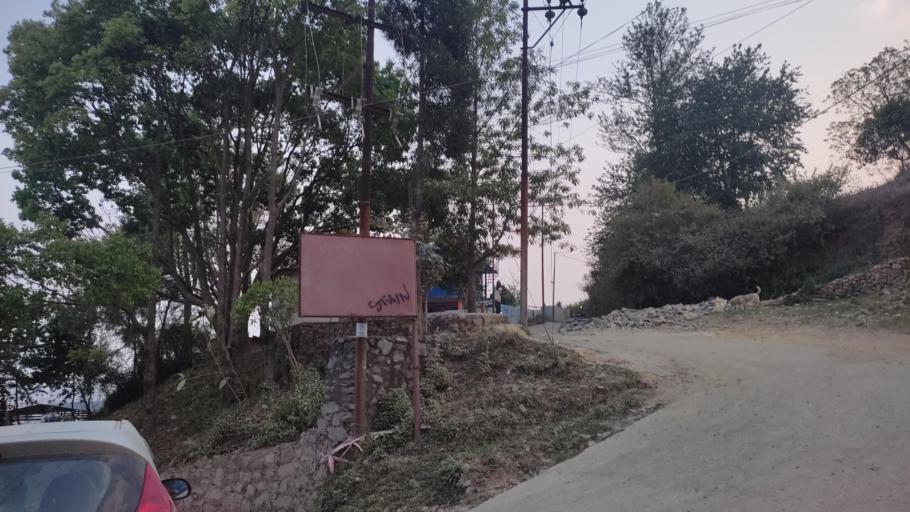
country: NP
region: Central Region
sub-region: Bagmati Zone
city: Patan
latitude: 27.6645
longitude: 85.2939
